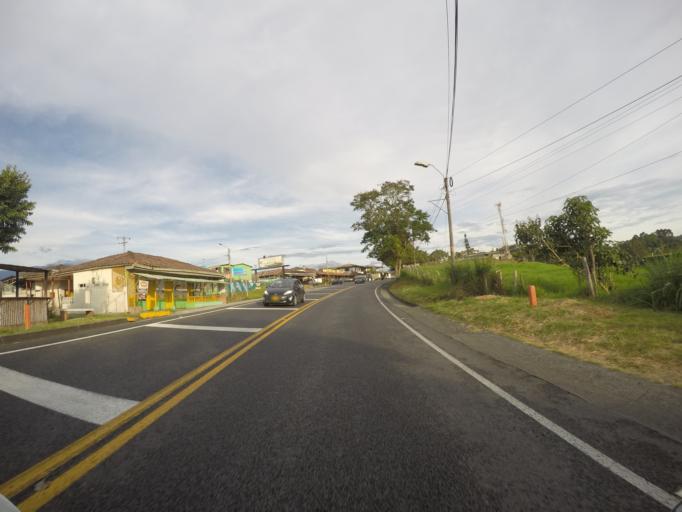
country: CO
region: Risaralda
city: Pereira
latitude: 4.7777
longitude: -75.6935
